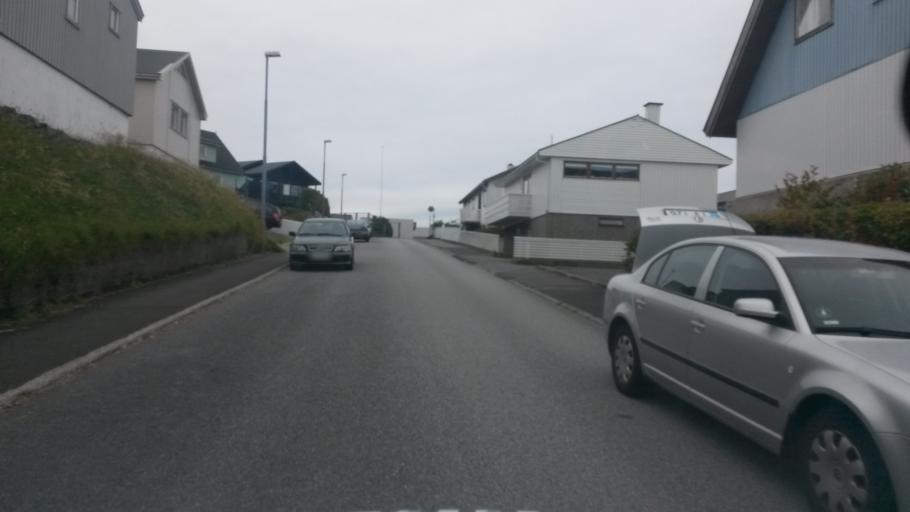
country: FO
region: Streymoy
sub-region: Torshavn
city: Torshavn
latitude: 62.0125
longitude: -6.7633
